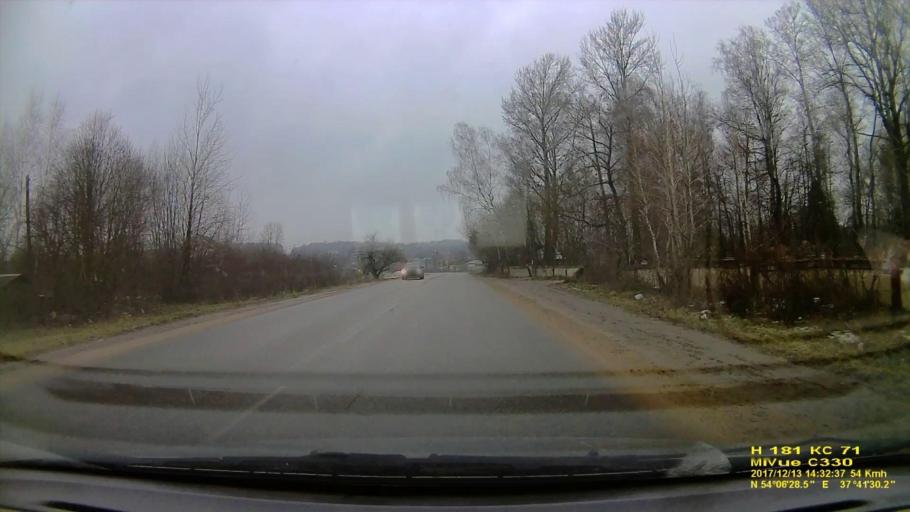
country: RU
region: Tula
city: Skuratovskiy
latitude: 54.1080
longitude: 37.6916
